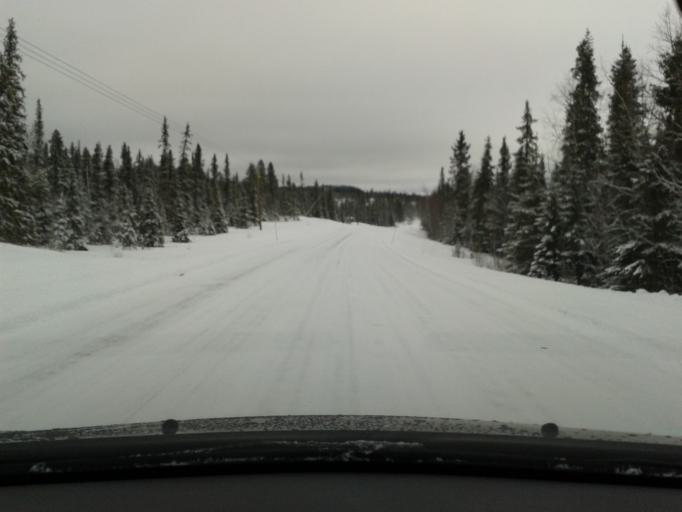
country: SE
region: Vaesterbotten
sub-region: Vilhelmina Kommun
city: Sjoberg
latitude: 65.2333
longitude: 15.8531
